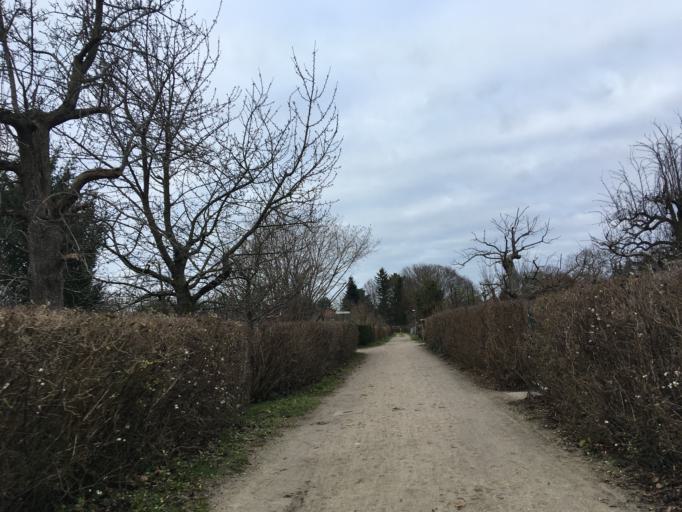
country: DE
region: Berlin
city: Niederschonhausen
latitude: 52.5780
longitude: 13.3914
